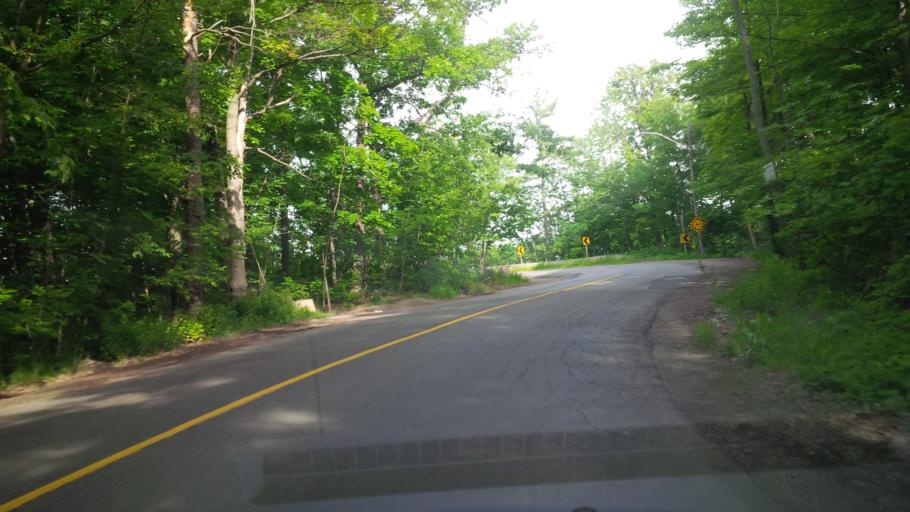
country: CA
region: Ontario
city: Burlington
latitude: 43.3382
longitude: -79.8664
